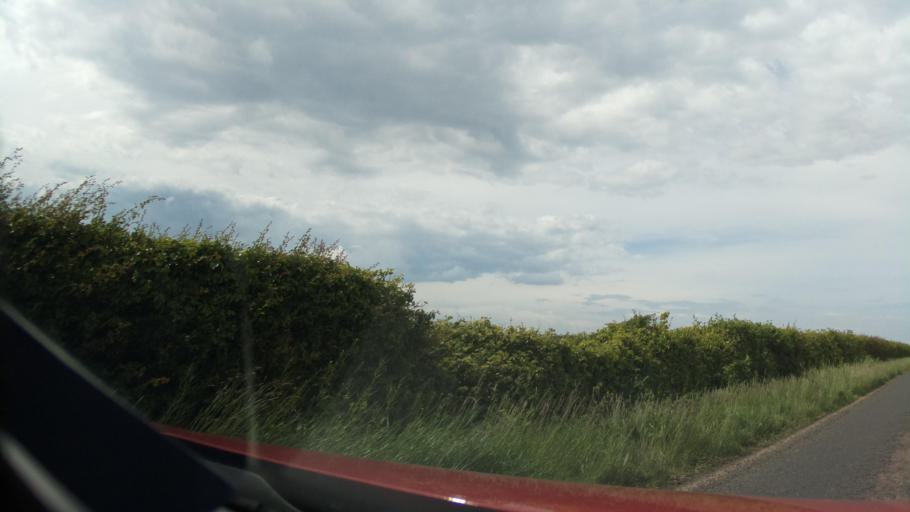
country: GB
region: England
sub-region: Northumberland
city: Ellingham
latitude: 55.4708
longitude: -1.7201
